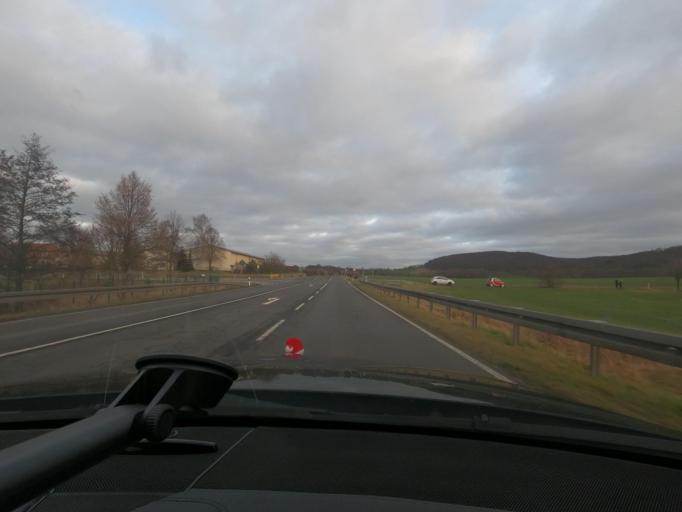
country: DE
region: Thuringia
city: Reinholterode
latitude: 51.3870
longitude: 10.1912
